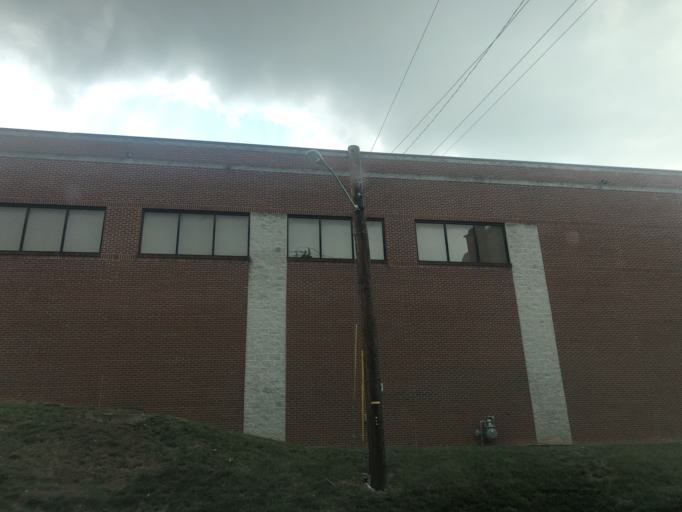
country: US
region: Tennessee
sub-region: Davidson County
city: Nashville
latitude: 36.1648
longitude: -86.8086
